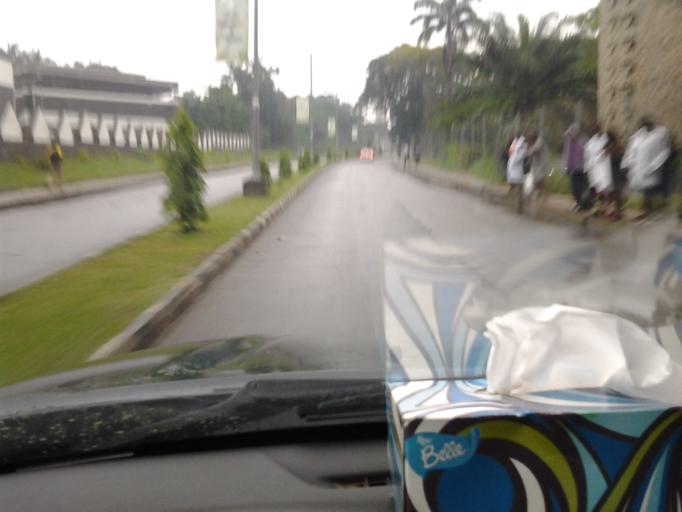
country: NG
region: Oyo
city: Ibadan
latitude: 7.4486
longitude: 3.9000
